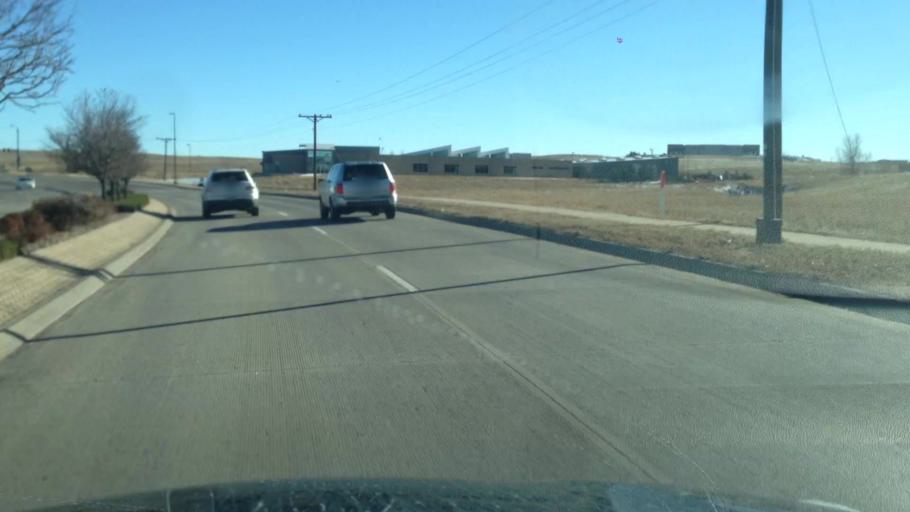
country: US
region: Colorado
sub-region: Arapahoe County
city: Dove Valley
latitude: 39.5839
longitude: -104.8145
